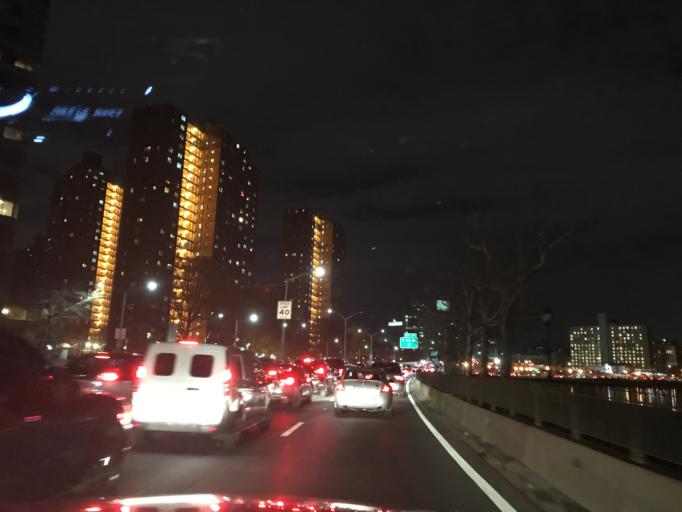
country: US
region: New York
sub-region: New York County
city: Manhattan
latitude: 40.7800
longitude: -73.9437
